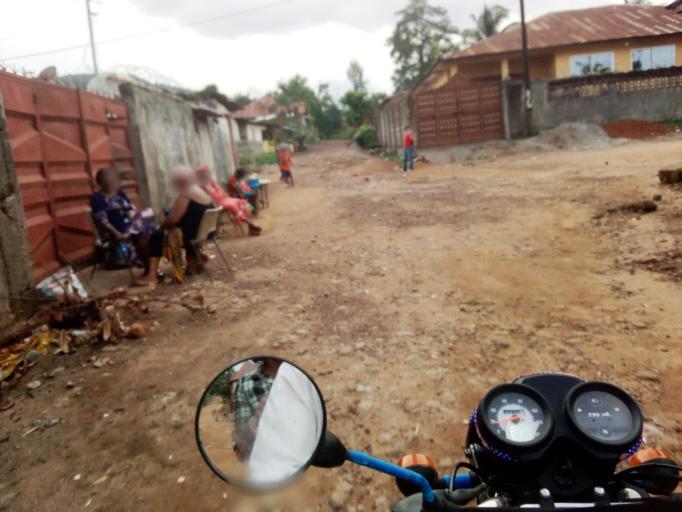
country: SL
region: Western Area
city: Waterloo
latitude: 8.3356
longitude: -13.0708
